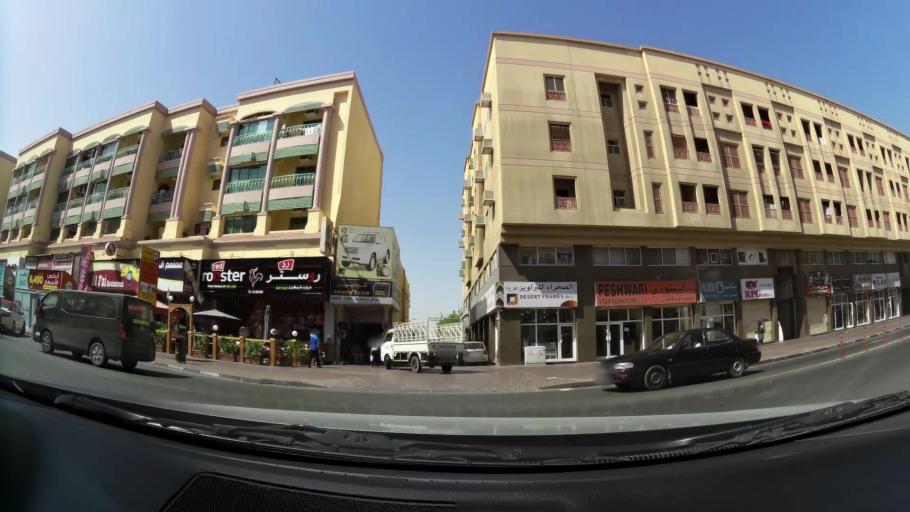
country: AE
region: Ash Shariqah
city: Sharjah
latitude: 25.2306
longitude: 55.2716
